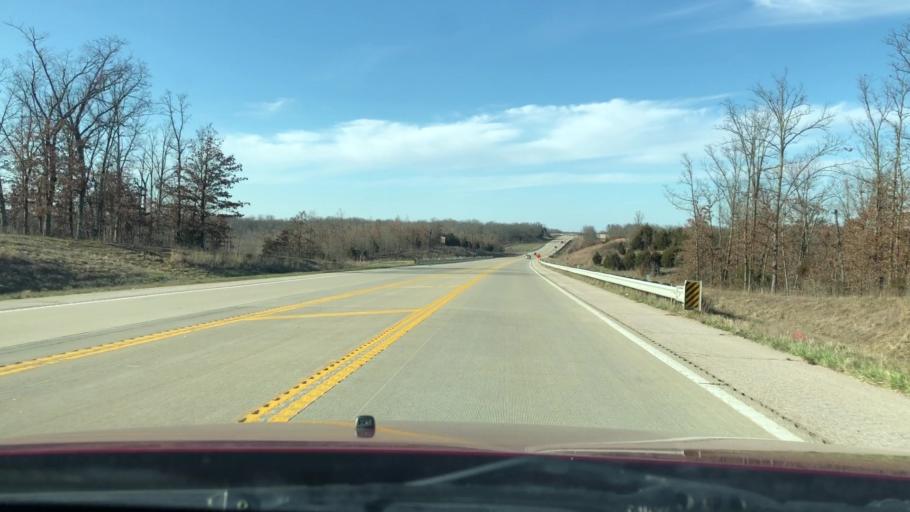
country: US
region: Missouri
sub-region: Camden County
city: Camdenton
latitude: 37.9391
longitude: -92.7155
